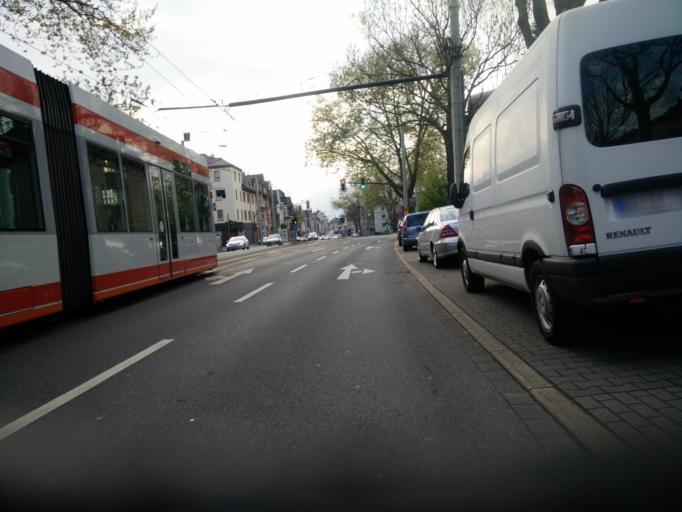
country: DE
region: North Rhine-Westphalia
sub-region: Regierungsbezirk Arnsberg
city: Bochum
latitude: 51.4729
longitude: 7.2425
